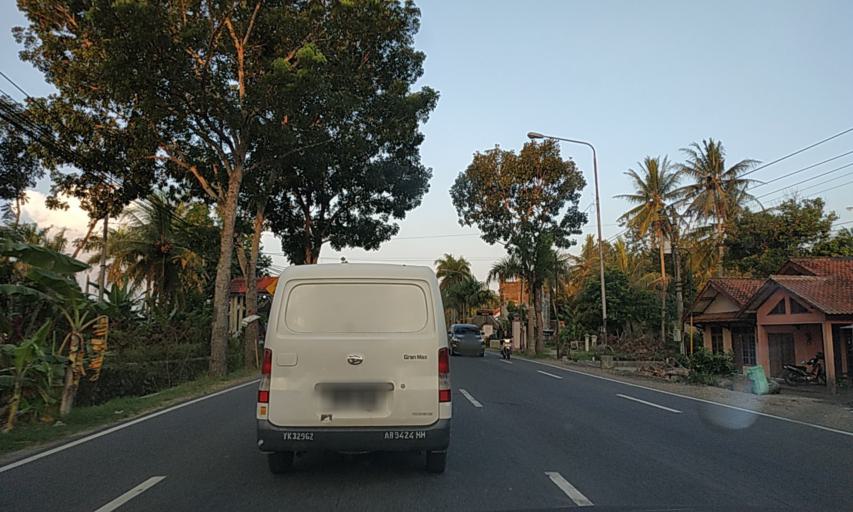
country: ID
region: Daerah Istimewa Yogyakarta
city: Srandakan
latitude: -7.8870
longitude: 110.0800
